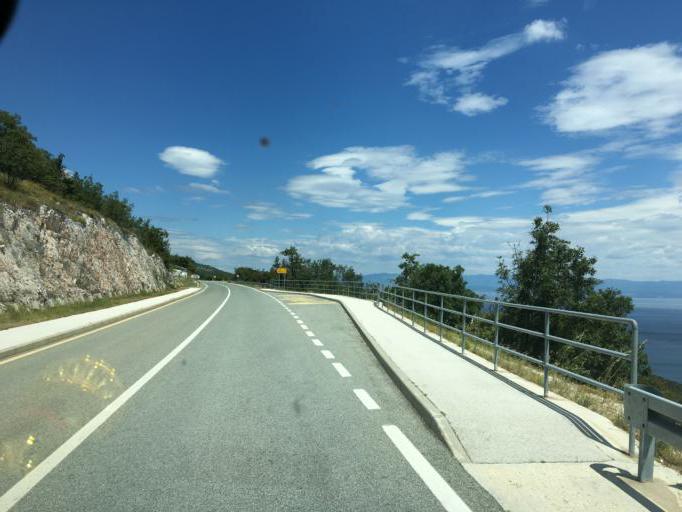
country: HR
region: Istarska
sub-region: Grad Labin
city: Rabac
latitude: 45.1411
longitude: 14.2126
